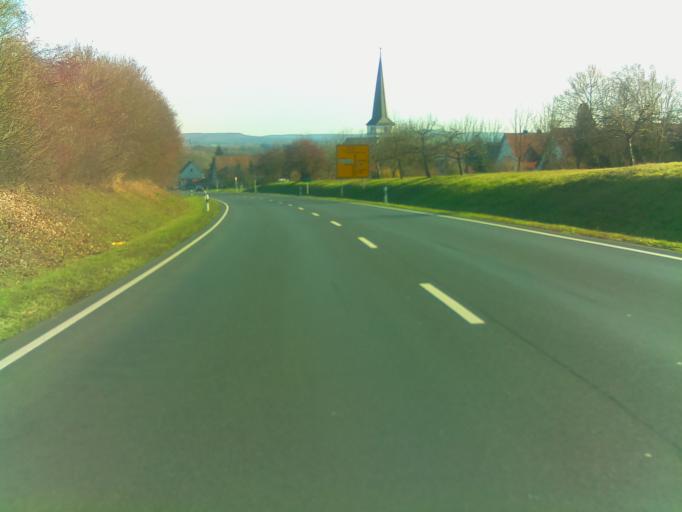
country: DE
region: Bavaria
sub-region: Regierungsbezirk Unterfranken
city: Grosseibstadt
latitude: 50.3029
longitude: 10.4063
